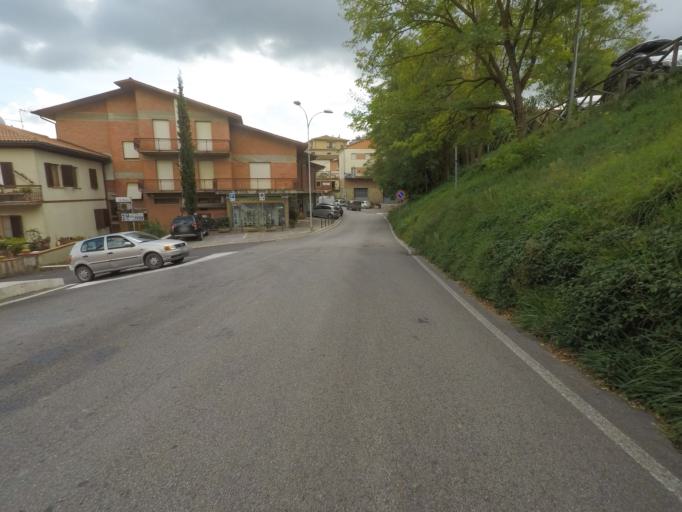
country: IT
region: Tuscany
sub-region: Provincia di Siena
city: Montepulciano
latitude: 43.1008
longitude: 11.7859
